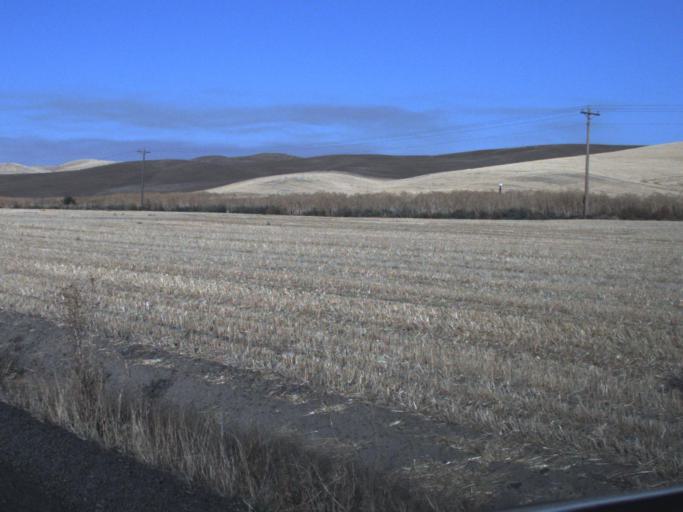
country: US
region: Washington
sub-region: Walla Walla County
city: Walla Walla
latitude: 46.1827
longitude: -118.3838
